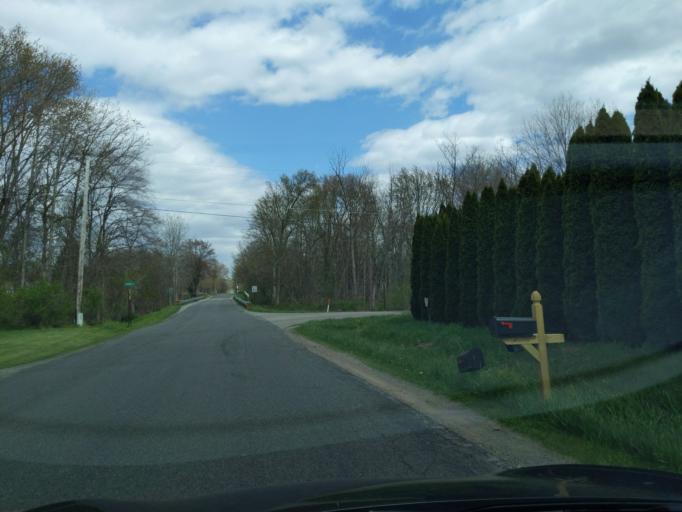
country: US
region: Michigan
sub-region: Ingham County
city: Mason
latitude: 42.6111
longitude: -84.4683
